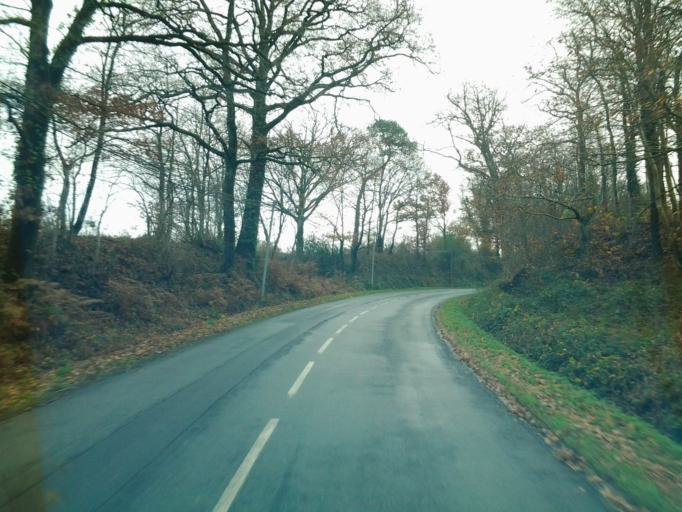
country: FR
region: Pays de la Loire
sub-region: Departement de la Vendee
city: La Roche-sur-Yon
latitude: 46.6585
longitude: -1.3967
